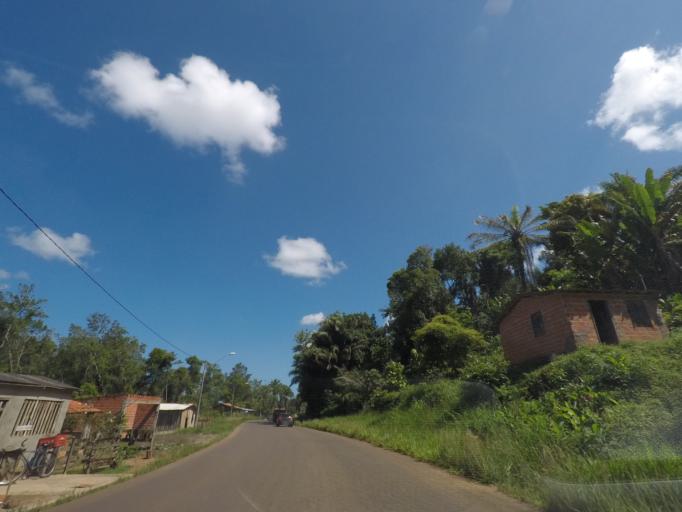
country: BR
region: Bahia
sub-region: Taperoa
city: Taperoa
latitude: -13.5964
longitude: -39.1064
